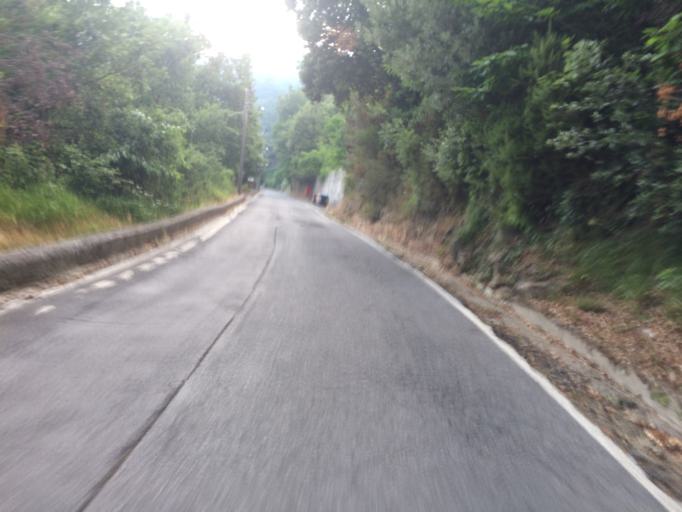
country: IT
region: Liguria
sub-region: Provincia di Imperia
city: Seborga
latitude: 43.8527
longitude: 7.7256
